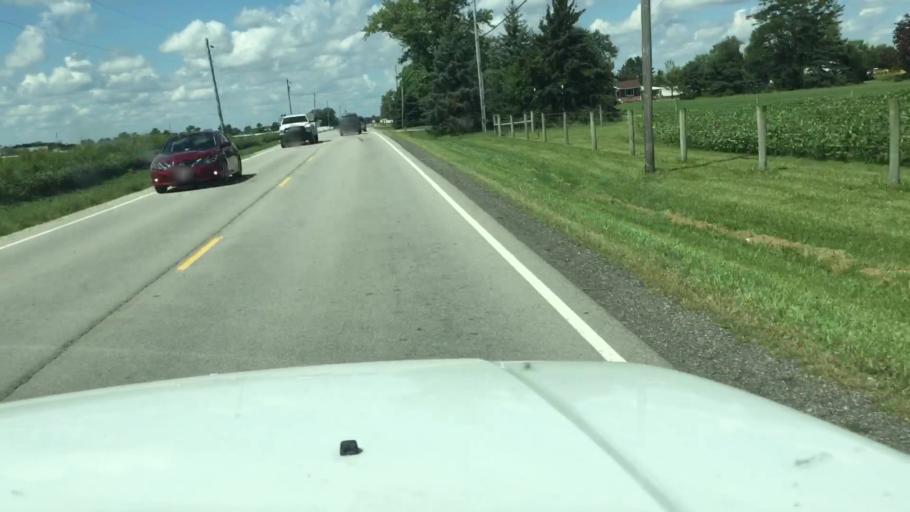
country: US
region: Ohio
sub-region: Madison County
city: Mount Sterling
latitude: 39.7426
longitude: -83.2796
